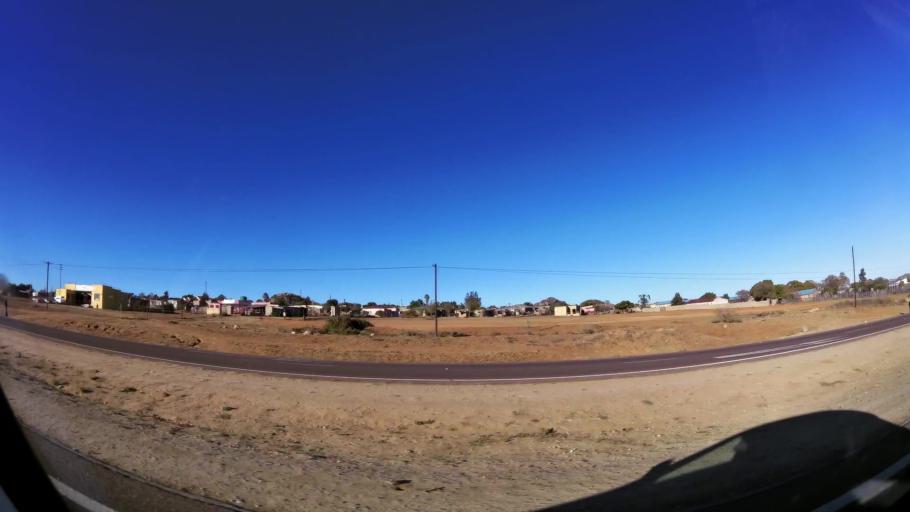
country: ZA
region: Limpopo
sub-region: Capricorn District Municipality
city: Mankoeng
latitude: -23.9081
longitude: 29.7680
